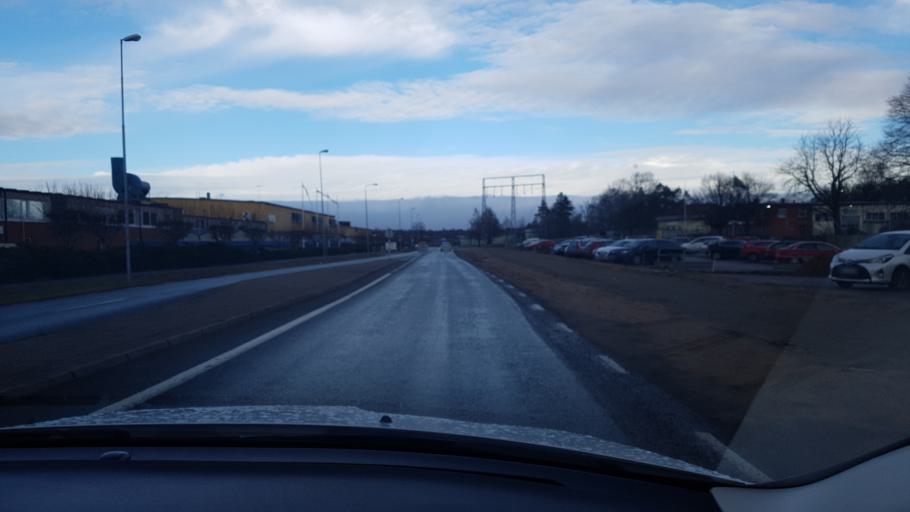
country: SE
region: Skane
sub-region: Hassleholms Kommun
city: Hassleholm
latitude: 56.1625
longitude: 13.7858
